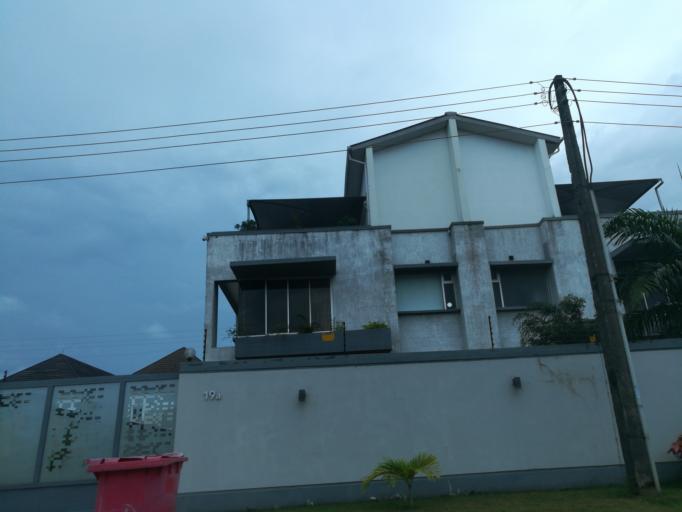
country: NG
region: Lagos
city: Ikoyi
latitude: 6.4403
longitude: 3.4799
